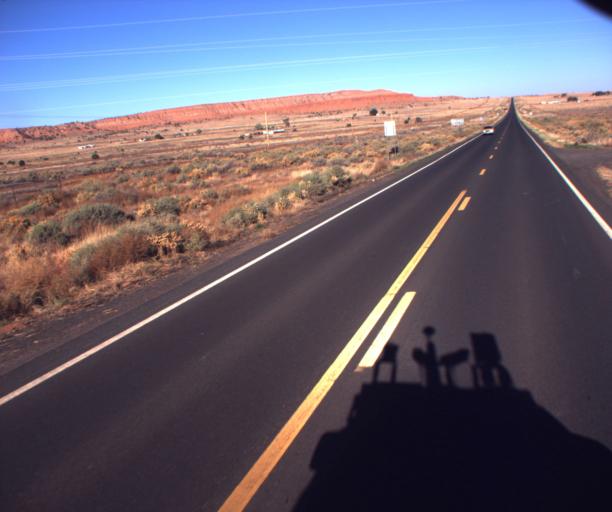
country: US
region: Arizona
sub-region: Apache County
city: Ganado
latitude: 35.7572
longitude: -109.6301
